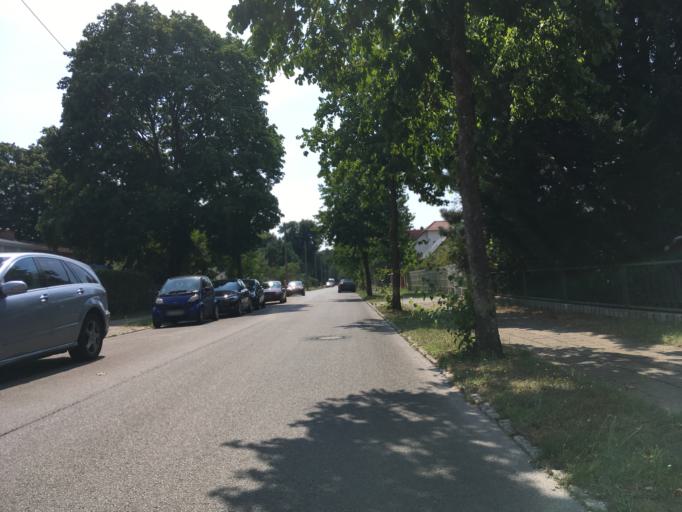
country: DE
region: Berlin
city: Friedrichshagen
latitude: 52.4754
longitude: 13.6090
